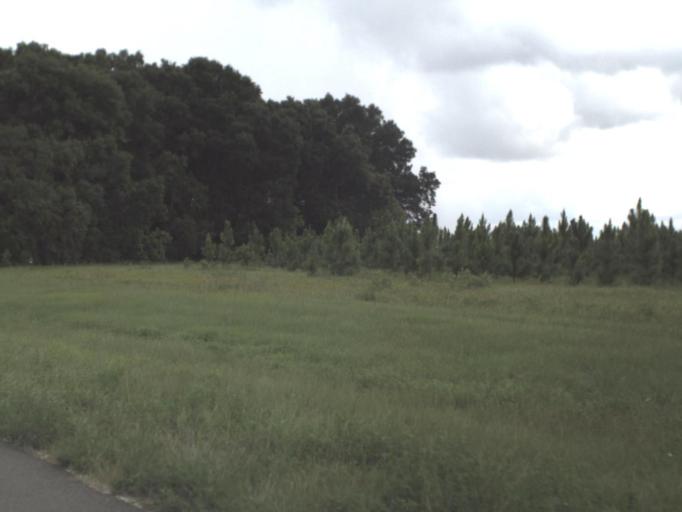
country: US
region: Florida
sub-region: Pasco County
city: Zephyrhills North
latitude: 28.3104
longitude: -82.1673
